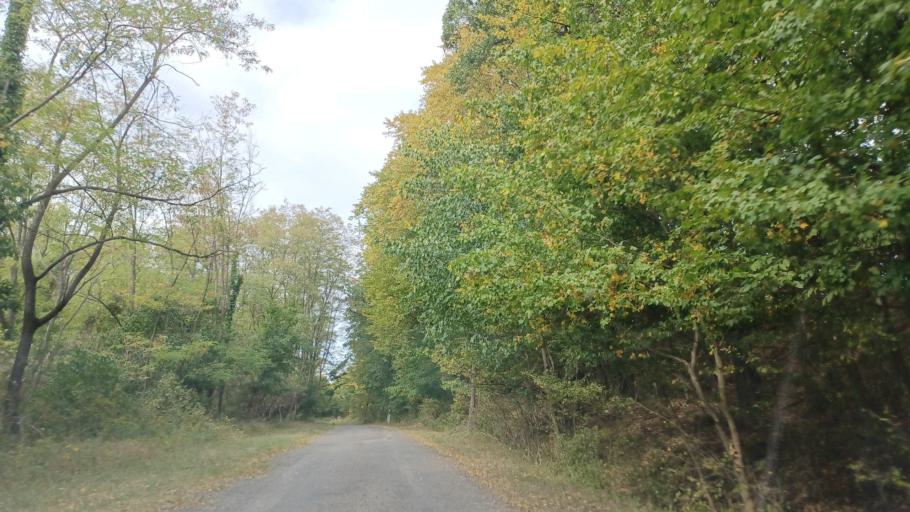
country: HU
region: Baranya
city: Mecseknadasd
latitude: 46.2032
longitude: 18.4531
